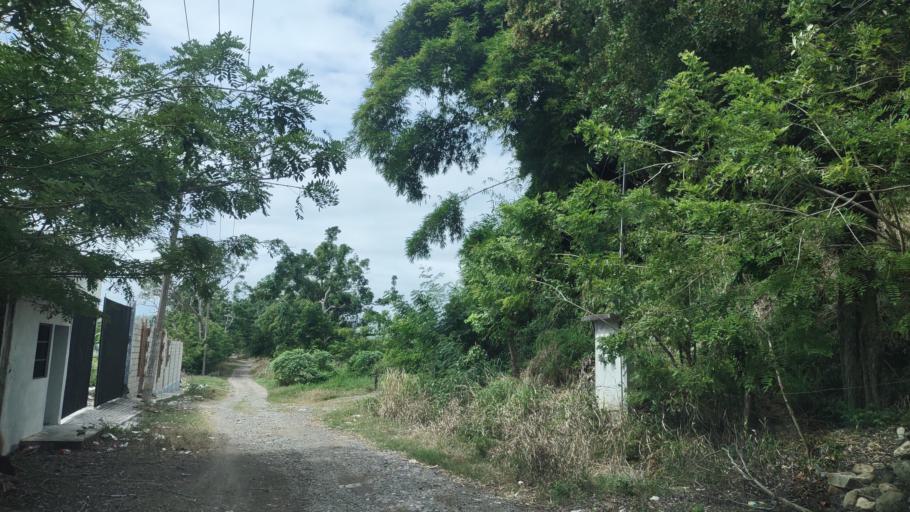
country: MX
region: Veracruz
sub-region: Papantla
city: Residencial Tajin
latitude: 20.5965
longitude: -97.4249
